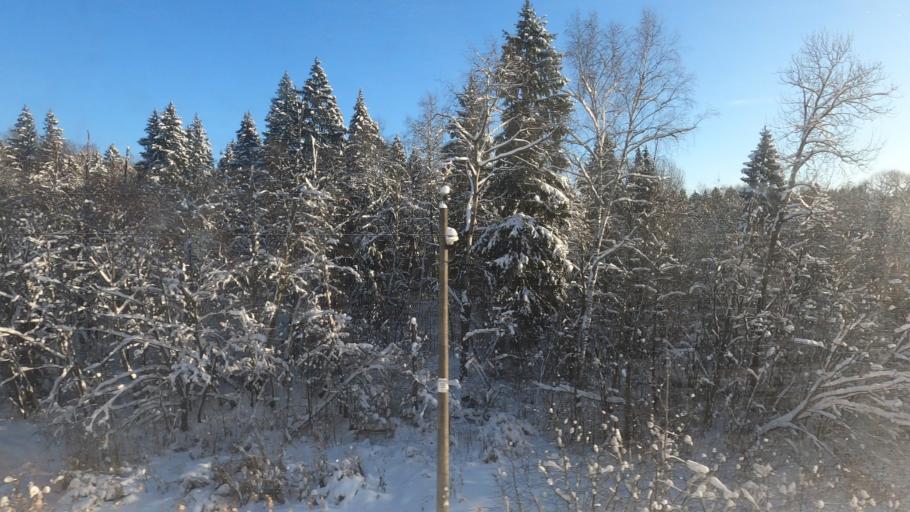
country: RU
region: Moskovskaya
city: Novo-Nikol'skoye
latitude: 56.5503
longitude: 37.5625
